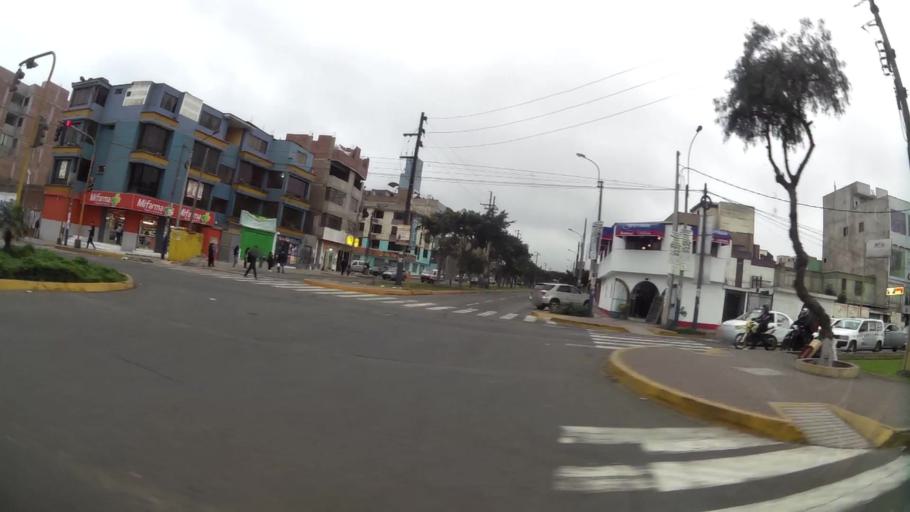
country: PE
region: Lima
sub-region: Lima
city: San Luis
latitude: -12.0748
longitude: -76.9825
